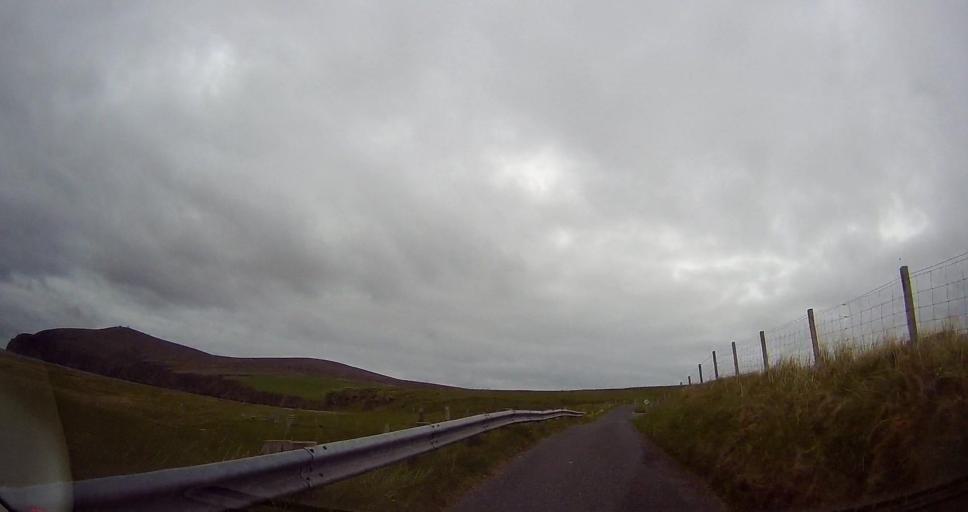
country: GB
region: Scotland
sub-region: Shetland Islands
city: Shetland
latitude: 60.8024
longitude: -0.8817
